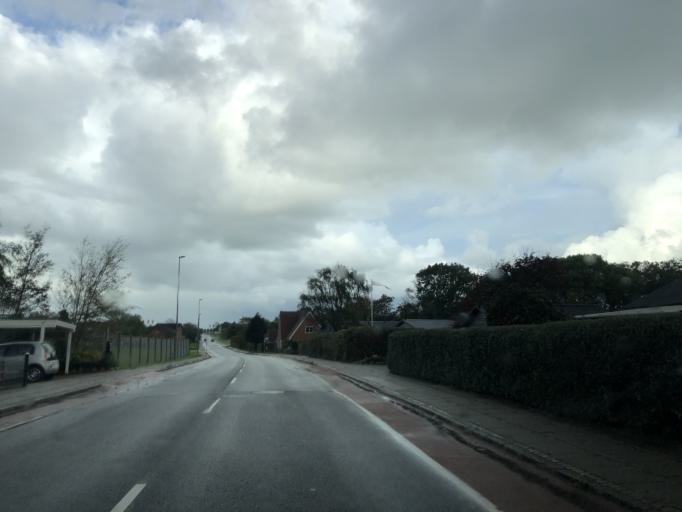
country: DK
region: Central Jutland
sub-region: Lemvig Kommune
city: Lemvig
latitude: 56.5471
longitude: 8.2897
